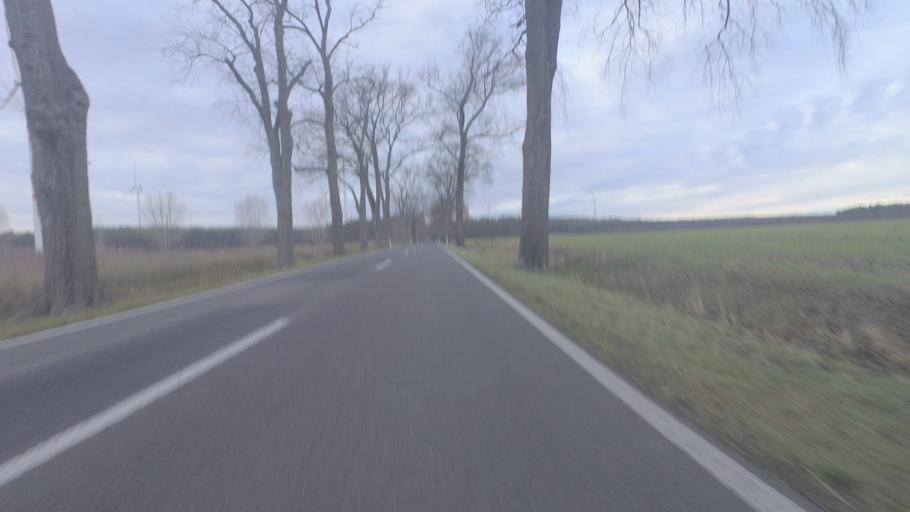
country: DE
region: Brandenburg
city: Sperenberg
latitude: 52.1965
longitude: 13.3146
